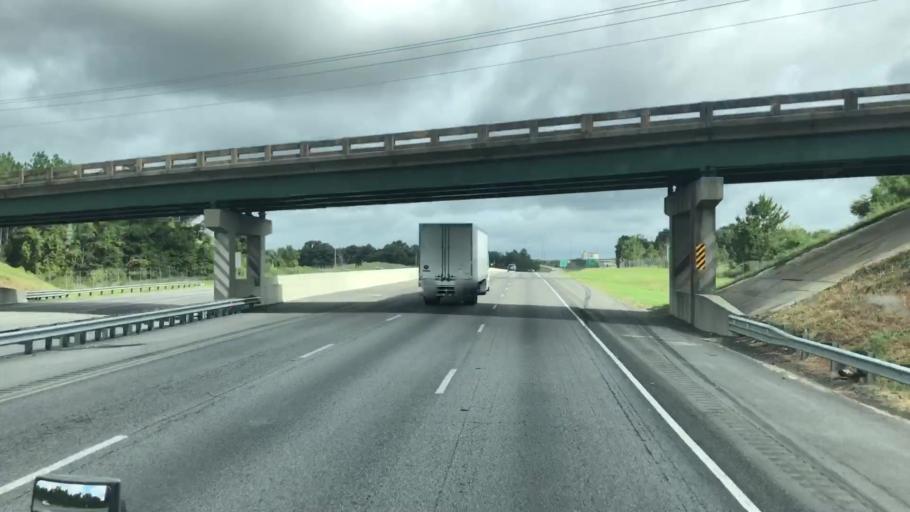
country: US
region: Georgia
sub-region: Crisp County
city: Cordele
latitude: 31.9259
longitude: -83.7449
